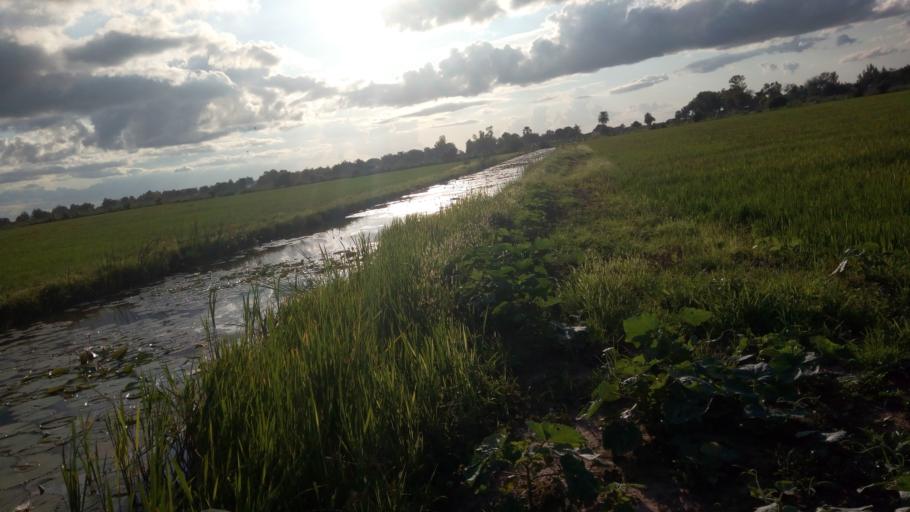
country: ML
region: Segou
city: Niono
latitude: 14.3064
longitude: -5.9544
